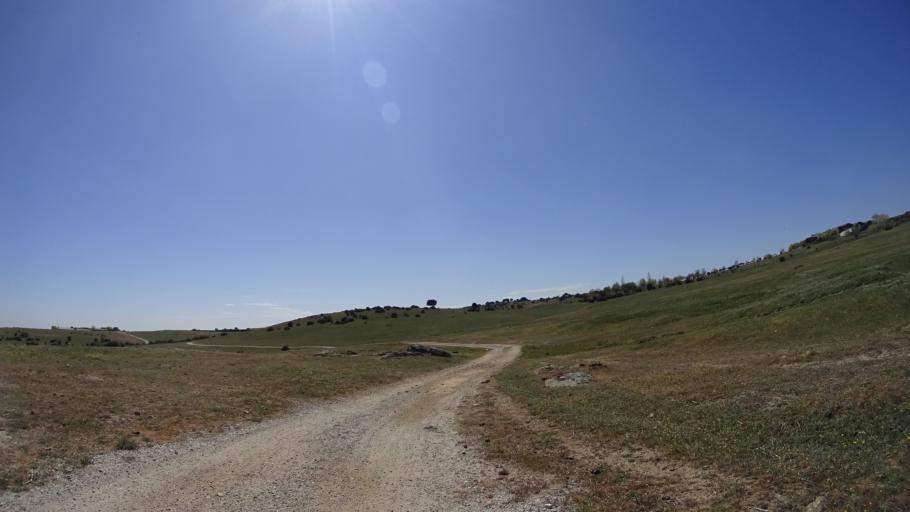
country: ES
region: Madrid
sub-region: Provincia de Madrid
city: Colmenar Viejo
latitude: 40.6951
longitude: -3.7573
